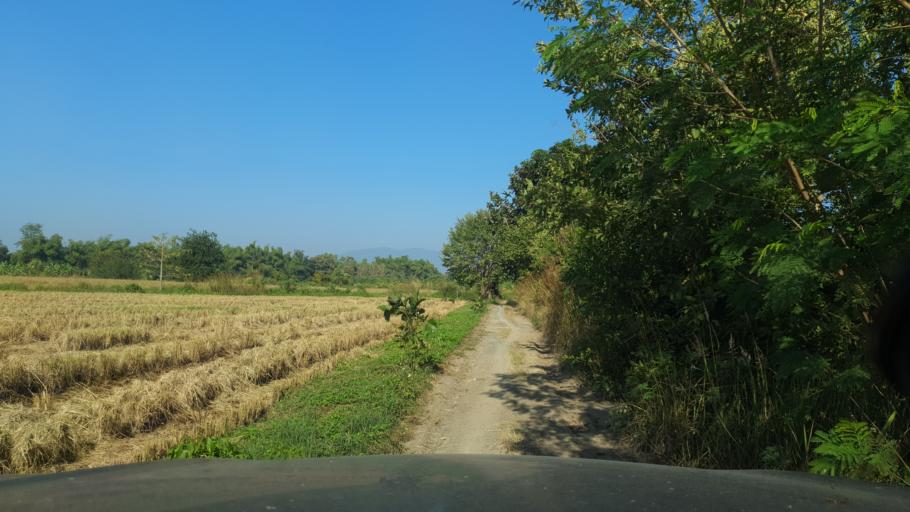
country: TH
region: Chiang Mai
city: Saraphi
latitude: 18.7123
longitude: 99.0776
